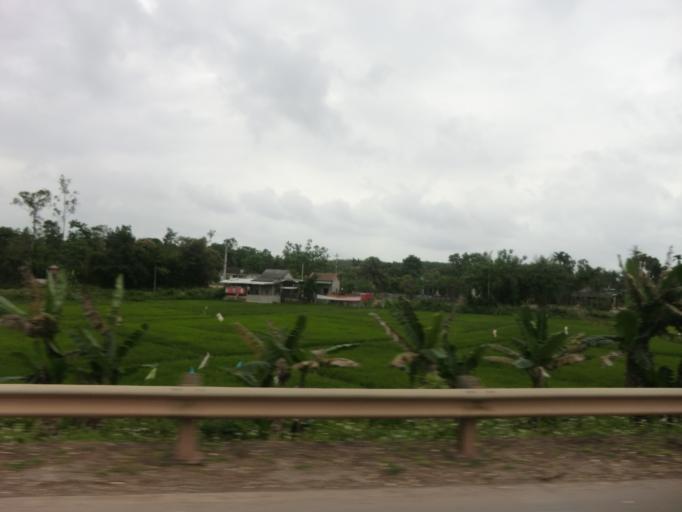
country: VN
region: Quang Tri
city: Cam Lo
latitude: 16.8261
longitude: 107.0051
